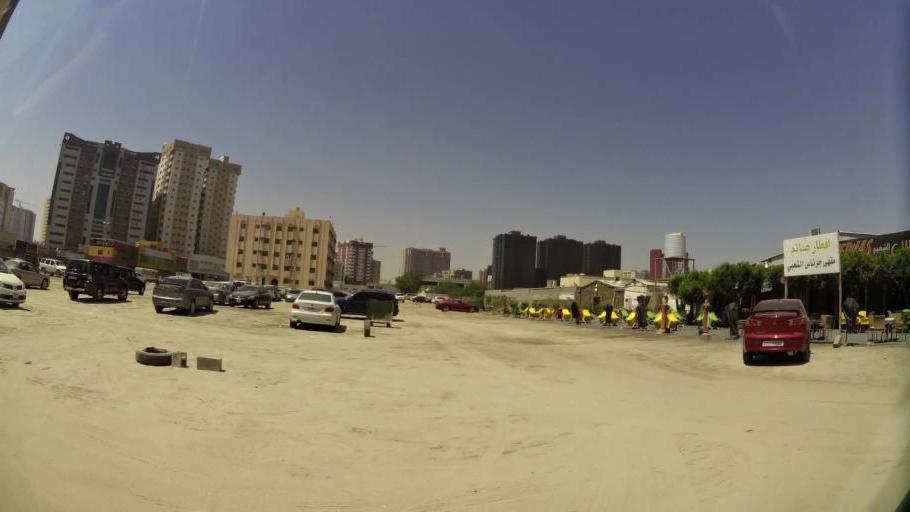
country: AE
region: Ajman
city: Ajman
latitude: 25.3925
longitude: 55.4655
